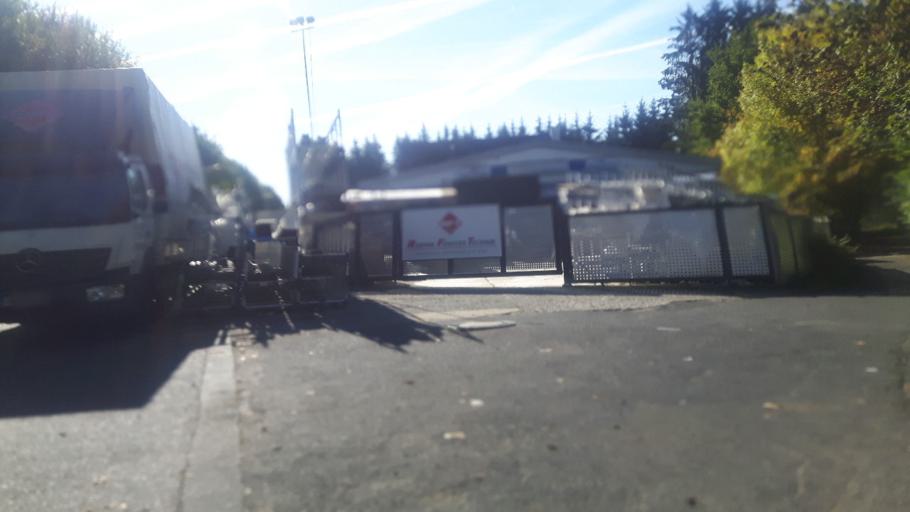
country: DE
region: Rheinland-Pfalz
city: Niederirsen
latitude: 50.8014
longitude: 7.6050
